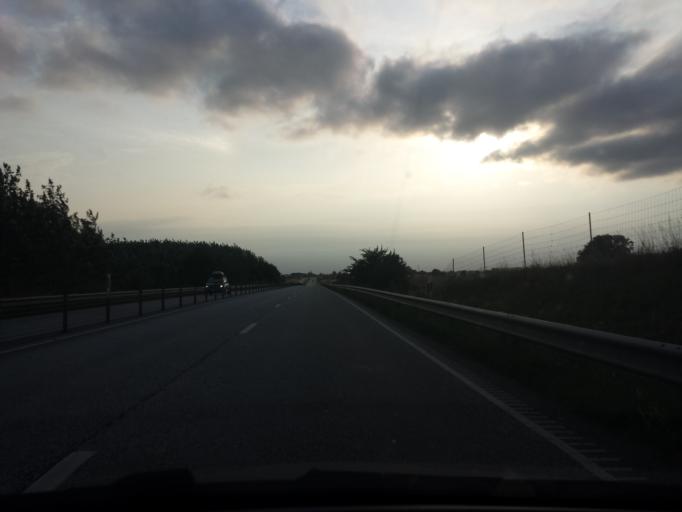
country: SE
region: Skane
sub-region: Svedala Kommun
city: Svedala
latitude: 55.5152
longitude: 13.2865
